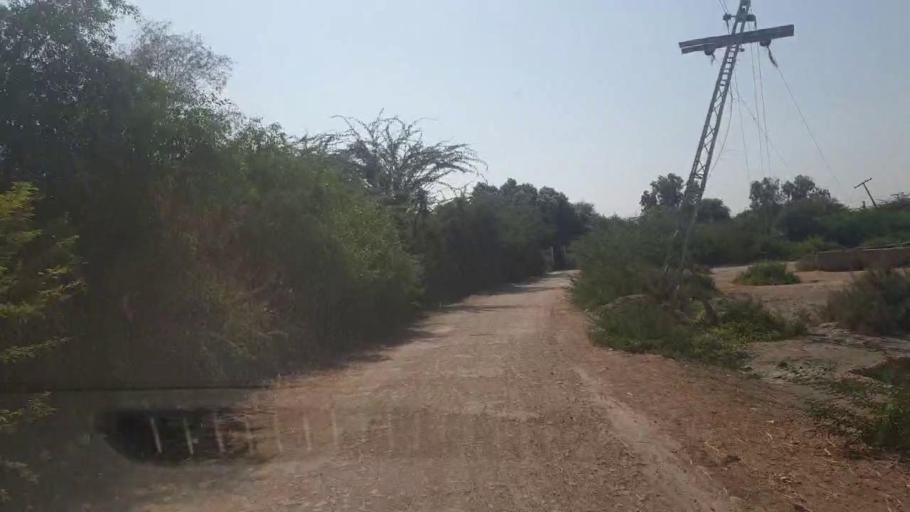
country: PK
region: Sindh
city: Badin
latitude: 24.6382
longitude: 68.9141
